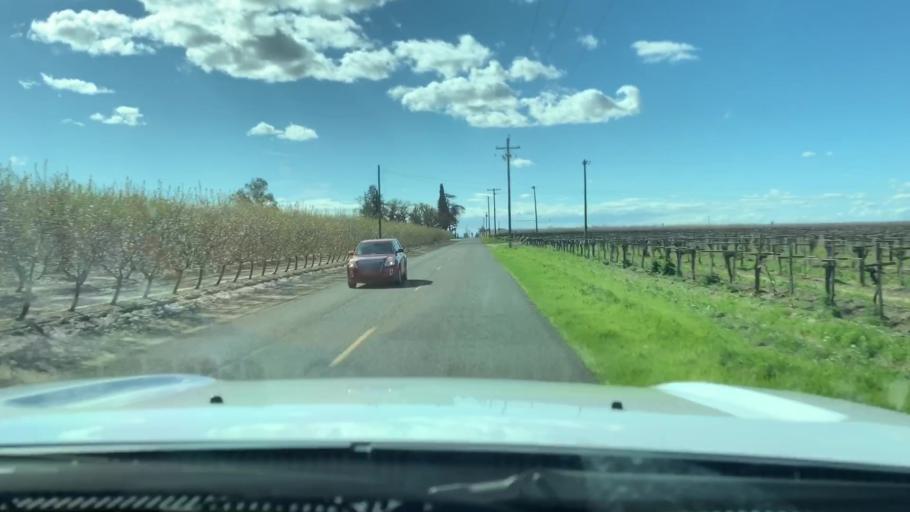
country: US
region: California
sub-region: Fresno County
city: Fowler
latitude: 36.5618
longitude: -119.7218
